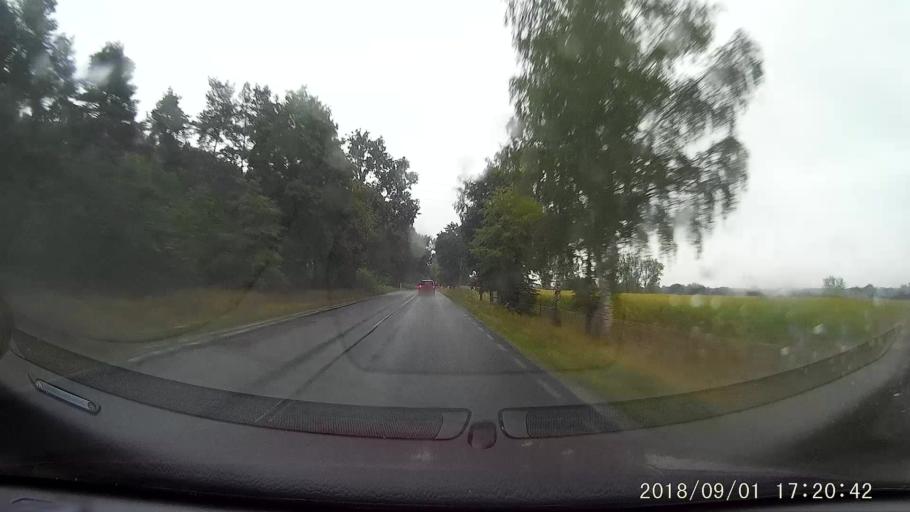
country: PL
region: Lubusz
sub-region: Powiat zielonogorski
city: Nowogrod Bobrzanski
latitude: 51.7218
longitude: 15.2811
